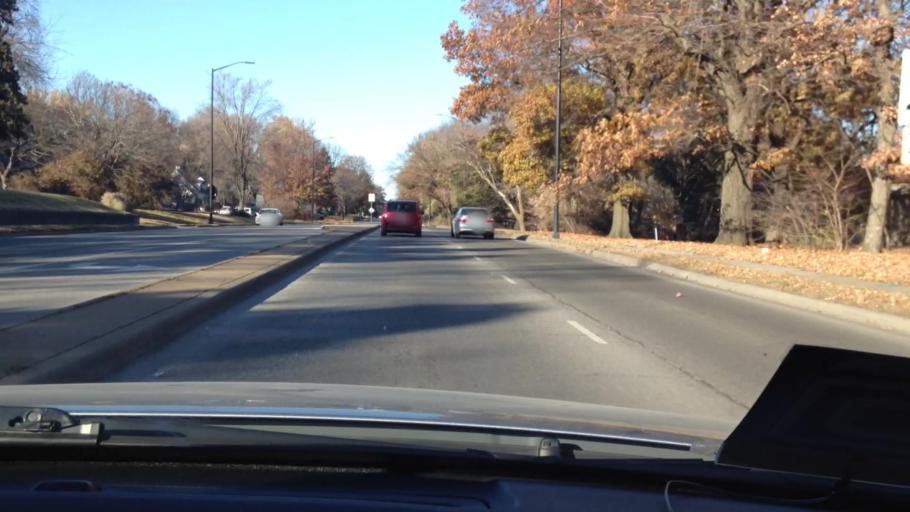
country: US
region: Kansas
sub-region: Johnson County
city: Overland Park
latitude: 39.0007
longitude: -94.6677
